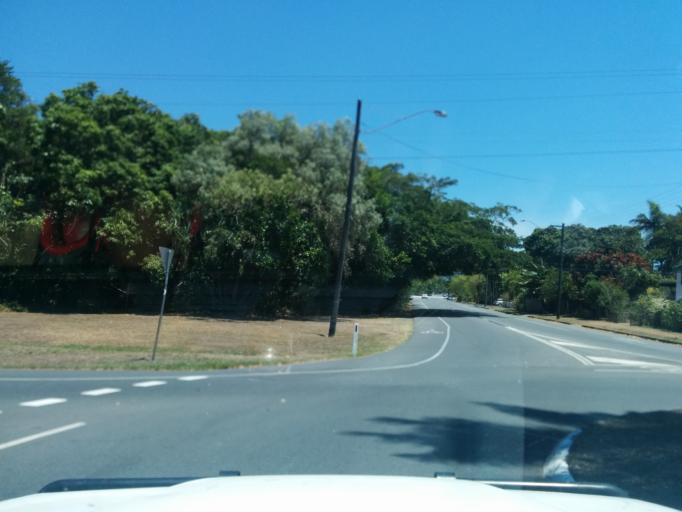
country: AU
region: Queensland
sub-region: Cairns
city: Cairns
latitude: -16.9202
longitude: 145.7603
